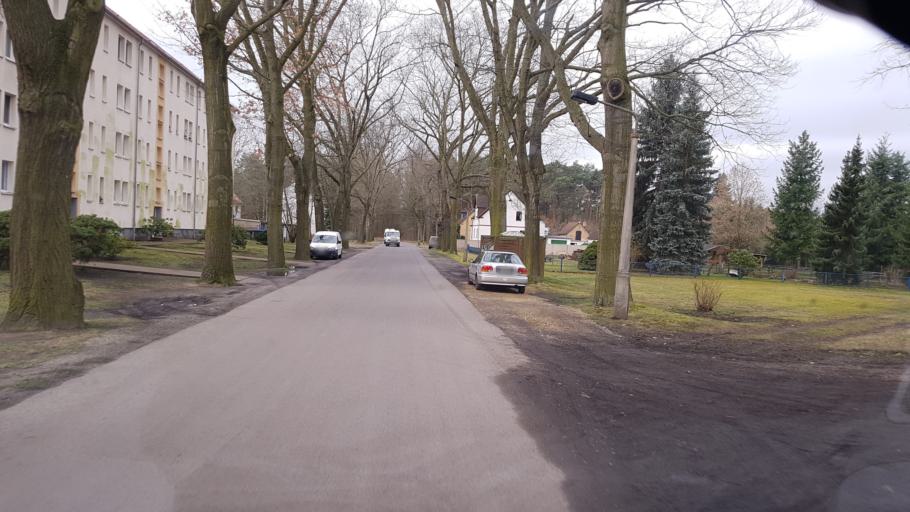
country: DE
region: Brandenburg
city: Ruhland
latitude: 51.4551
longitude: 13.8520
